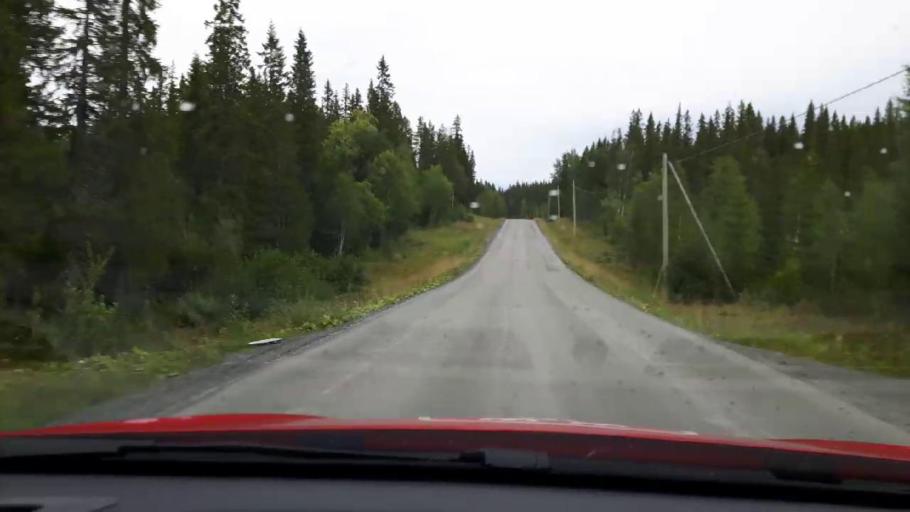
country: SE
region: Jaemtland
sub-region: Are Kommun
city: Jarpen
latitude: 63.4302
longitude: 13.3117
